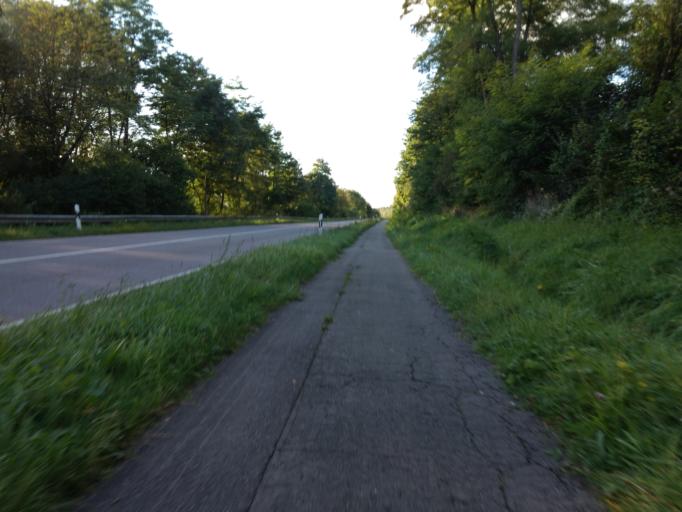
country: DE
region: Saarland
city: Rehlingen-Siersburg
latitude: 49.3934
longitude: 6.6689
